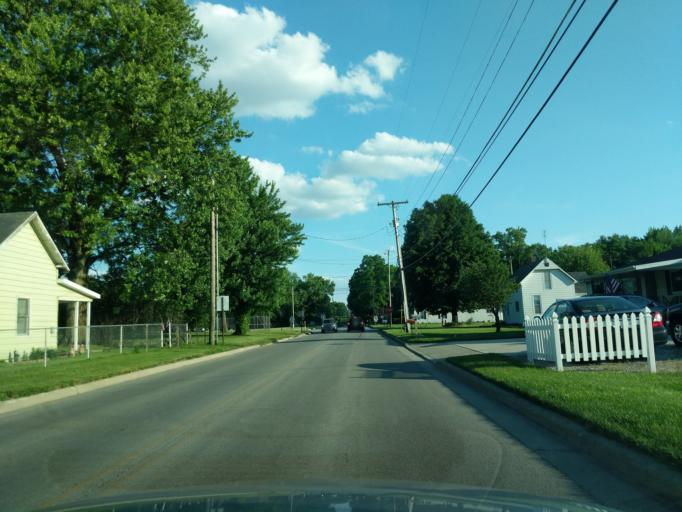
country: US
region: Indiana
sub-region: Huntington County
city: Huntington
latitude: 40.8752
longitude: -85.4710
